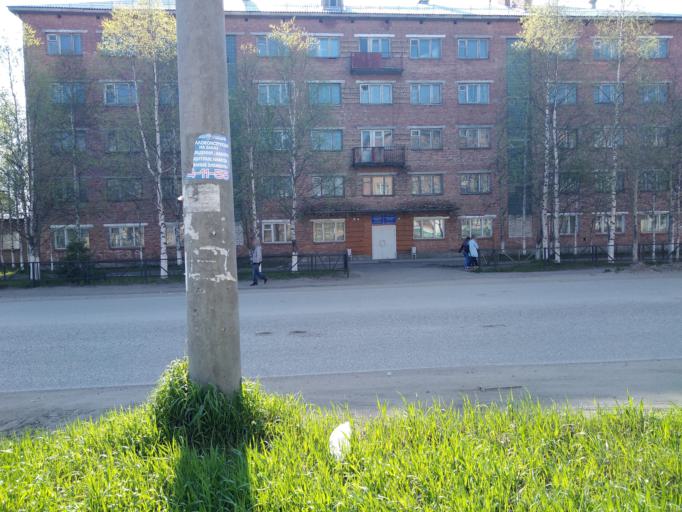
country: RU
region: Komi Republic
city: Pechora
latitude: 65.1241
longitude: 57.1543
